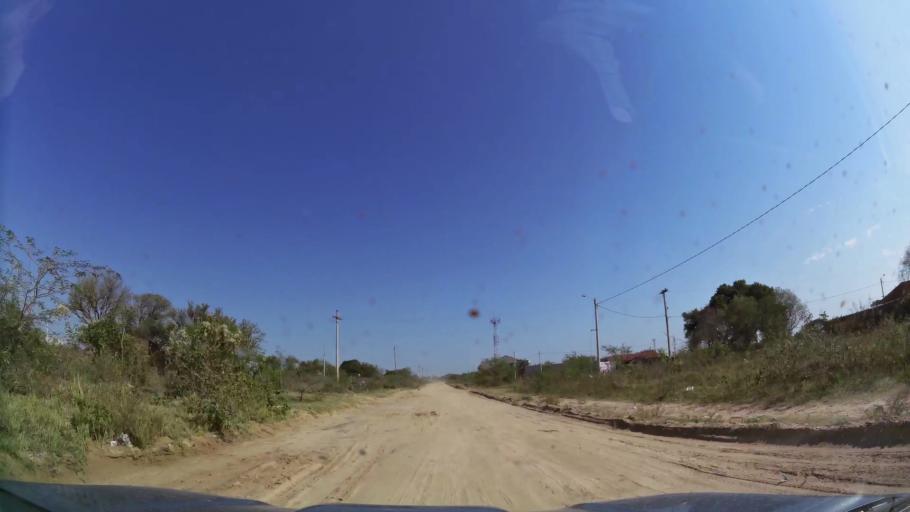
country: BO
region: Santa Cruz
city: Cotoca
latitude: -17.7258
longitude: -63.0701
